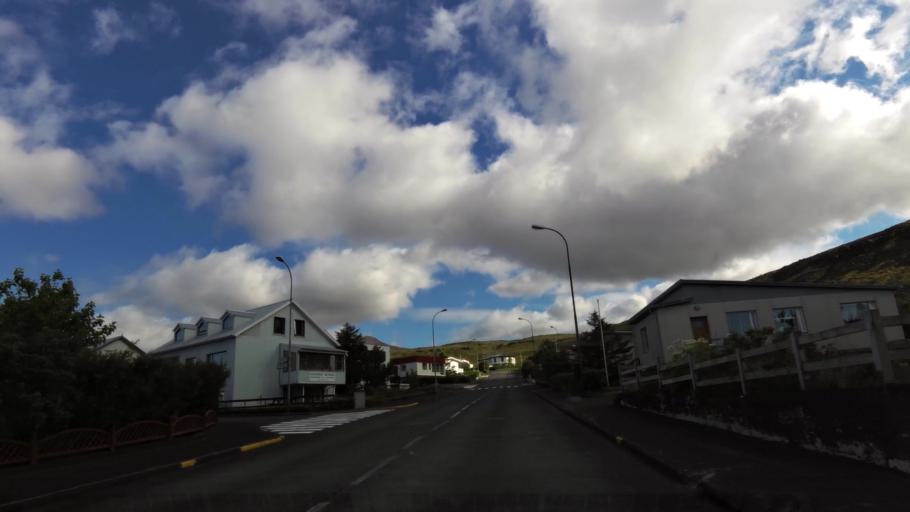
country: IS
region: West
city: Olafsvik
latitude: 64.8930
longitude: -23.7098
